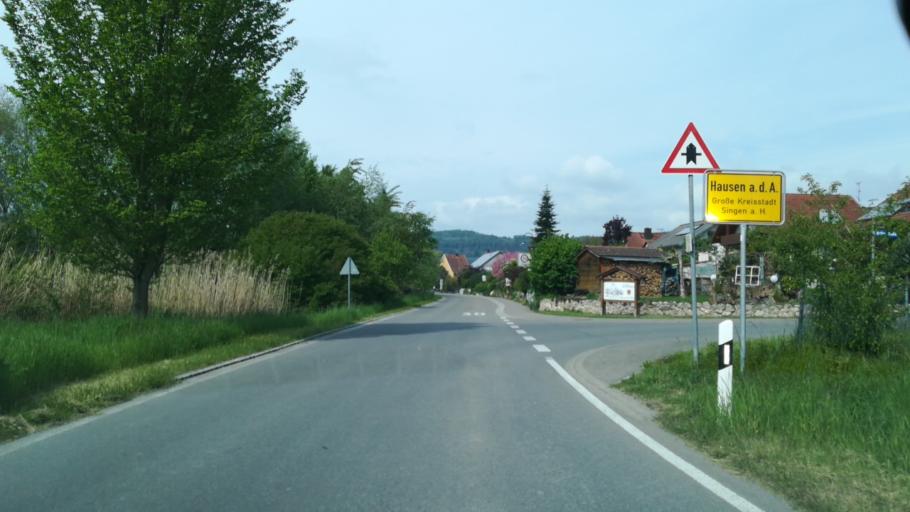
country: DE
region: Baden-Wuerttemberg
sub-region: Freiburg Region
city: Volkertshausen
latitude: 47.7917
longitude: 8.8463
